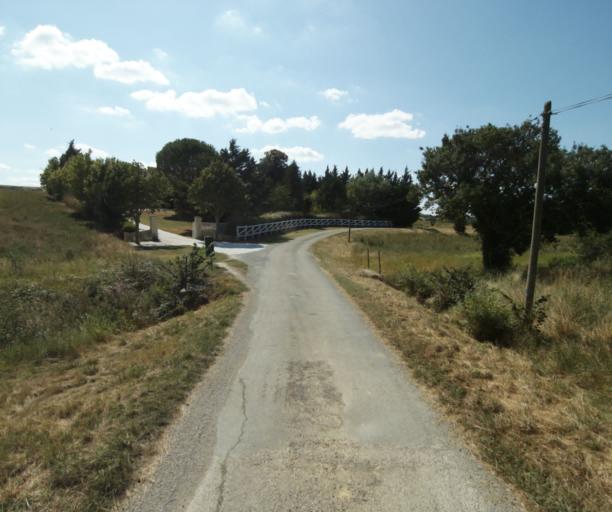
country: FR
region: Midi-Pyrenees
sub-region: Departement de la Haute-Garonne
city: Saint-Felix-Lauragais
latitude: 43.4765
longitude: 1.8902
